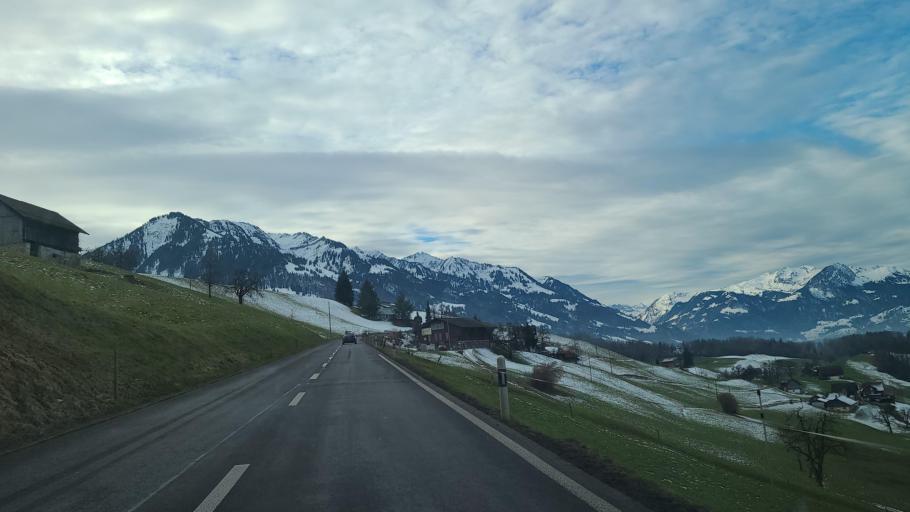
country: CH
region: Obwalden
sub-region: Obwalden
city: Kerns
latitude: 46.8928
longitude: 8.2777
